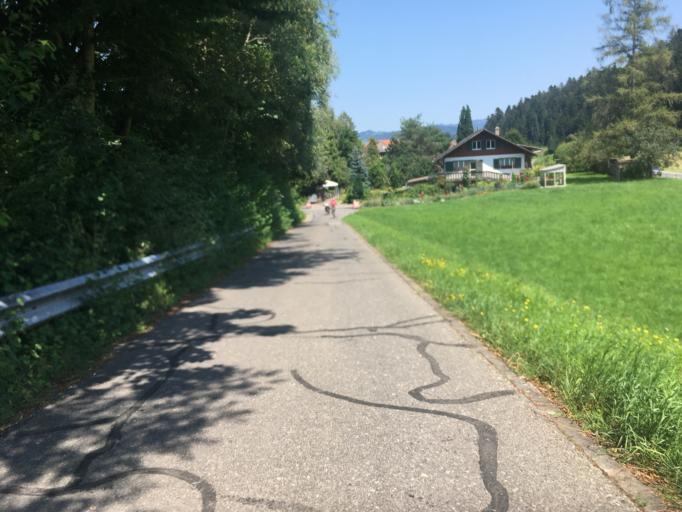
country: CH
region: Bern
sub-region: Emmental District
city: Signau
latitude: 46.9134
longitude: 7.7192
